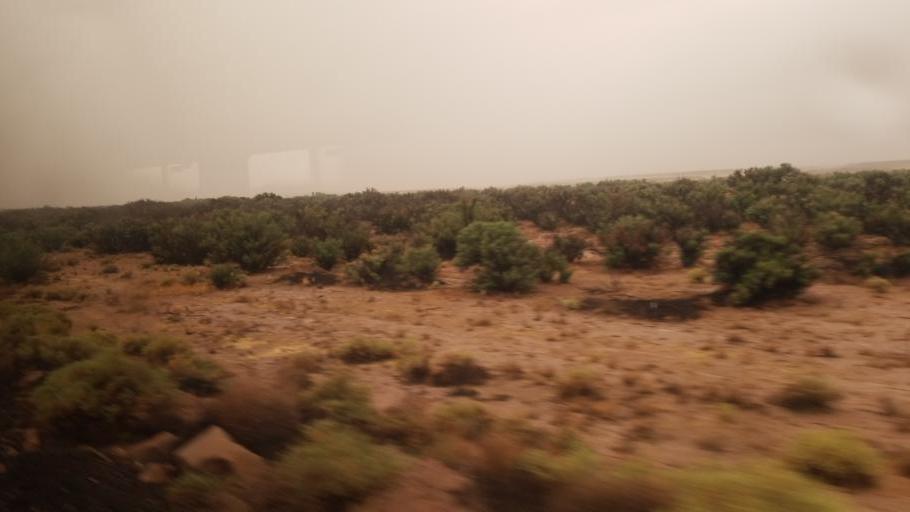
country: US
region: Arizona
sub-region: Navajo County
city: Joseph City
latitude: 34.9559
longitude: -110.3632
